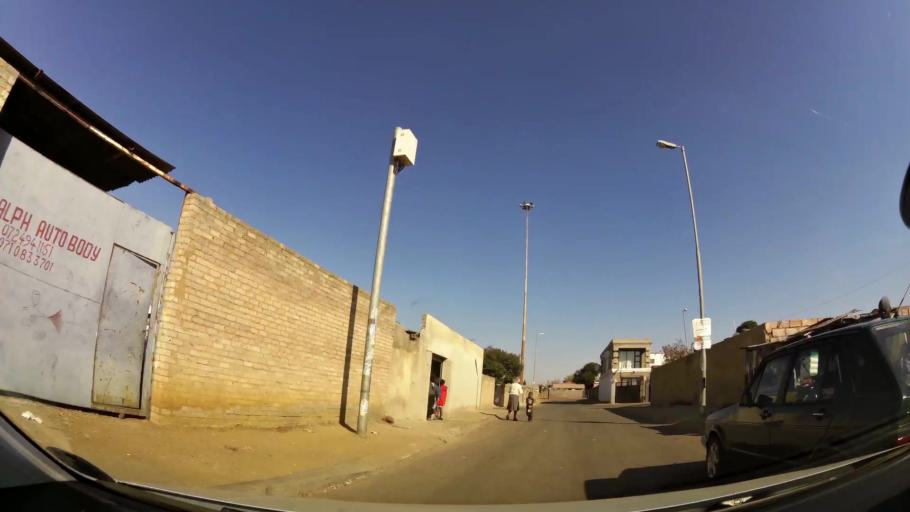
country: ZA
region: Gauteng
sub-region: City of Johannesburg Metropolitan Municipality
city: Soweto
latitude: -26.2792
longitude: 27.8735
